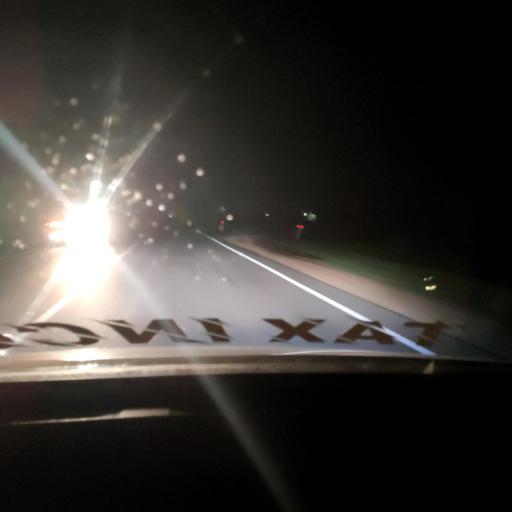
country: RU
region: Voronezj
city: Novovoronezh
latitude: 51.4136
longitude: 39.2996
